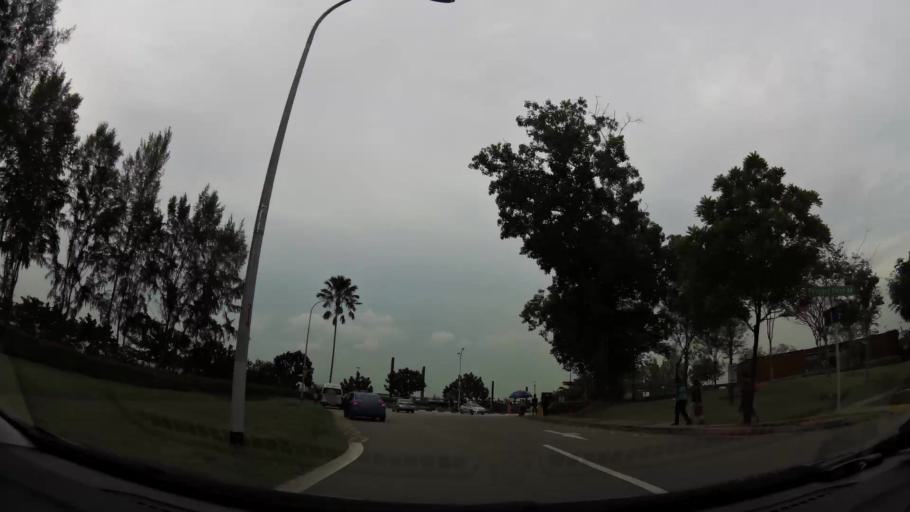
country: MY
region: Johor
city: Kampung Pasir Gudang Baru
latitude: 1.4208
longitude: 103.9105
